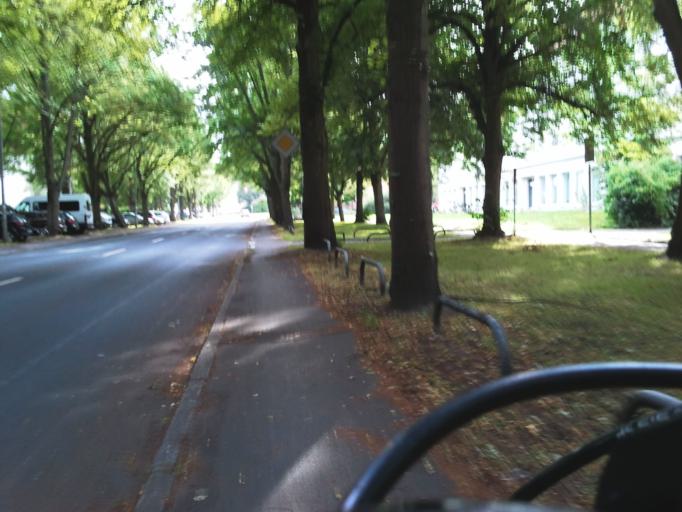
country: DE
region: Mecklenburg-Vorpommern
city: Rostock
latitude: 54.0916
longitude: 12.0910
